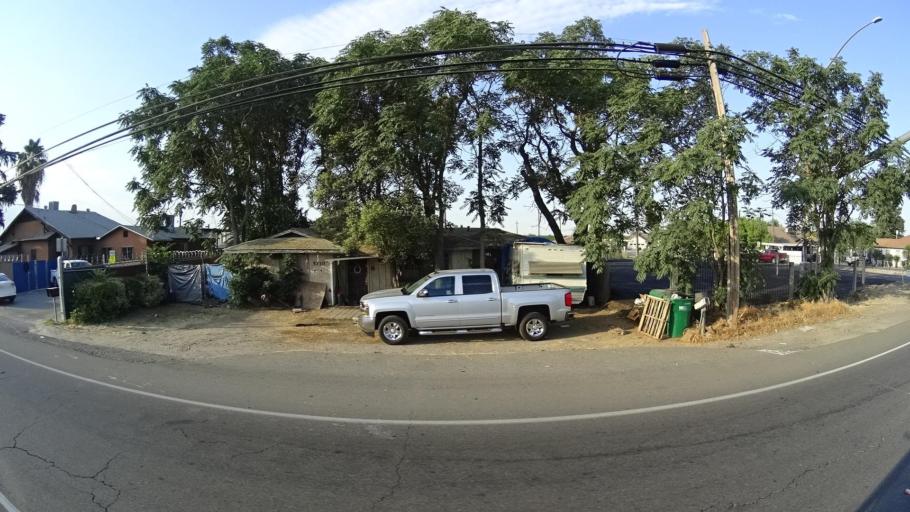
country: US
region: California
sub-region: Fresno County
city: Sunnyside
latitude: 36.7077
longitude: -119.7181
